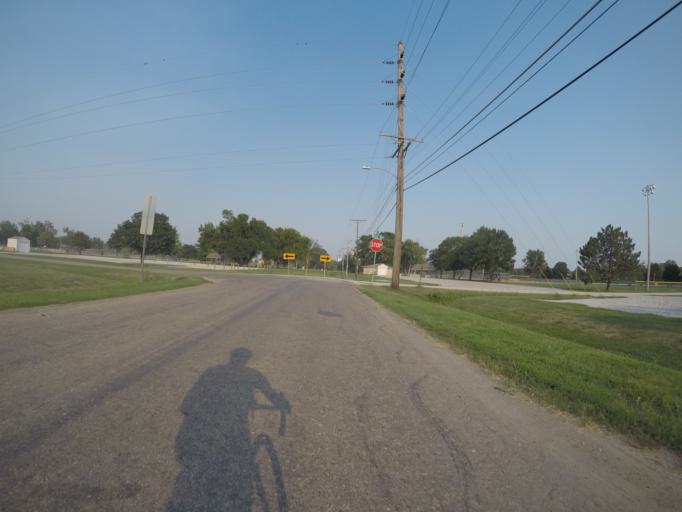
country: US
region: Nebraska
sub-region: Gage County
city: Beatrice
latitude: 40.2629
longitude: -96.7606
